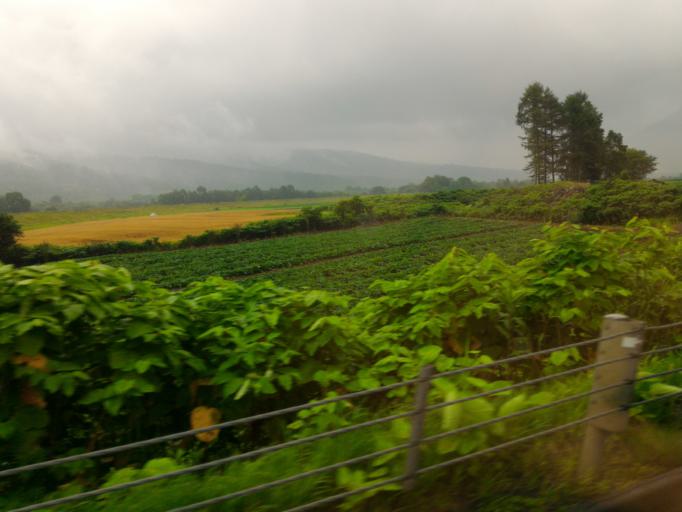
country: JP
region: Hokkaido
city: Nayoro
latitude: 44.5897
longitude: 142.3059
